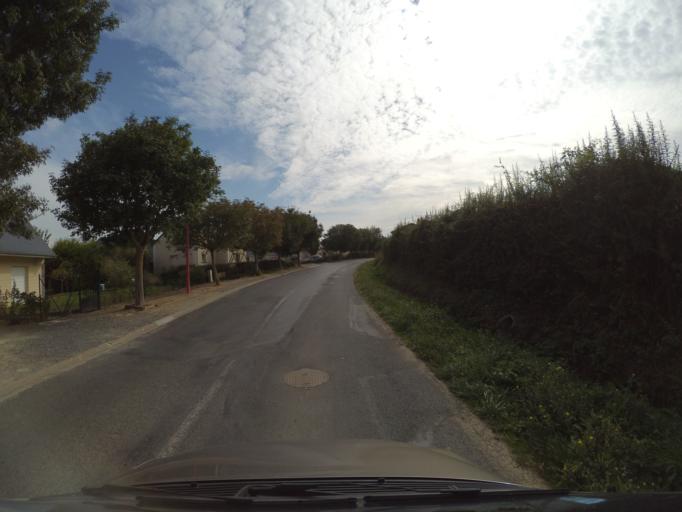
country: FR
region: Pays de la Loire
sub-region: Departement de Maine-et-Loire
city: Saint-Jean
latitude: 47.2003
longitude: -0.3717
